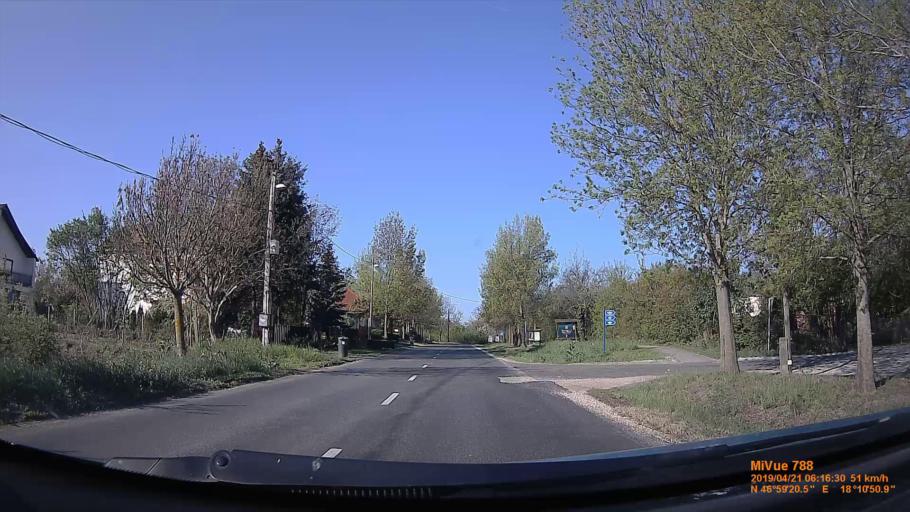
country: HU
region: Fejer
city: Lepseny
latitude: 46.9890
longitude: 18.1808
